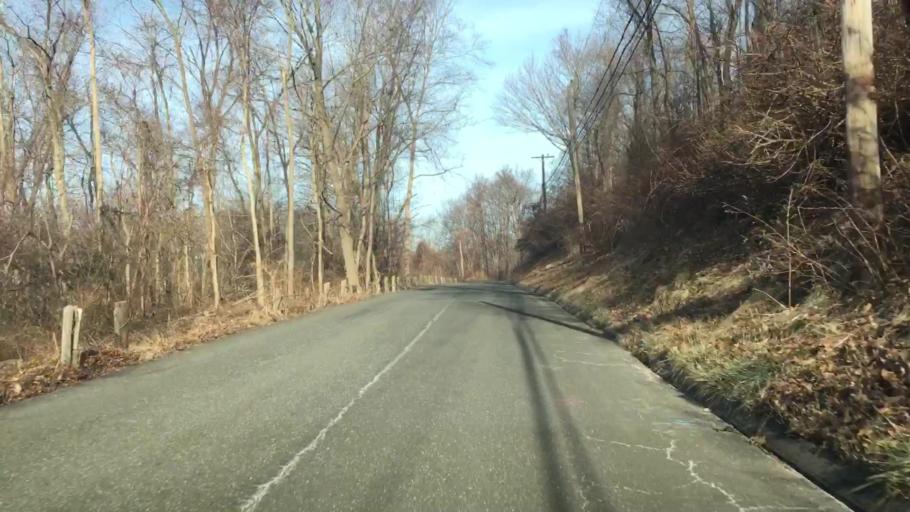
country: US
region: Connecticut
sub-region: Fairfield County
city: Danbury
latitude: 41.3695
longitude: -73.5038
